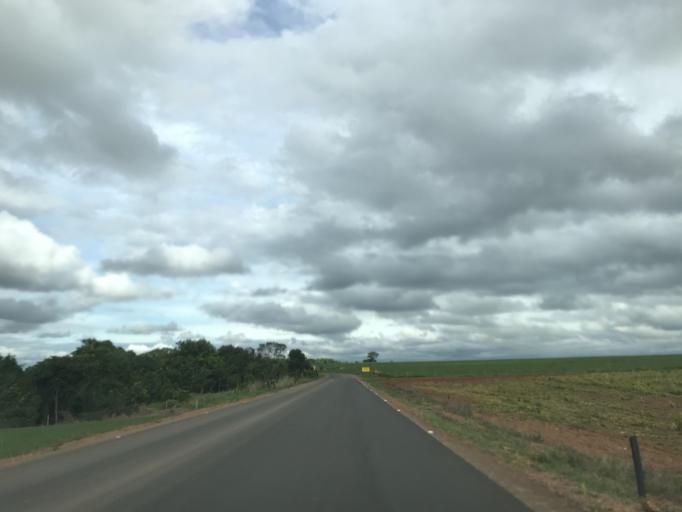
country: BR
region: Goias
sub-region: Vianopolis
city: Vianopolis
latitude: -16.9677
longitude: -48.6059
